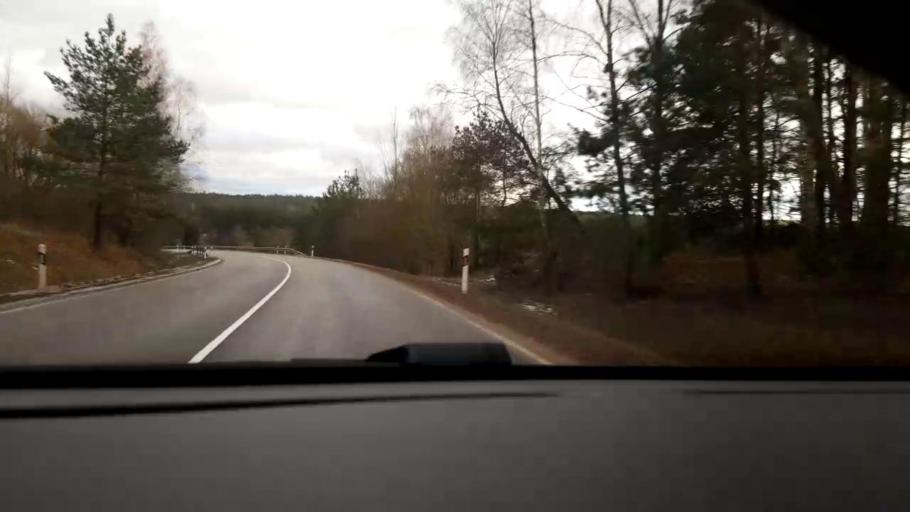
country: LT
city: Nemencine
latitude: 54.8648
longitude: 25.3944
